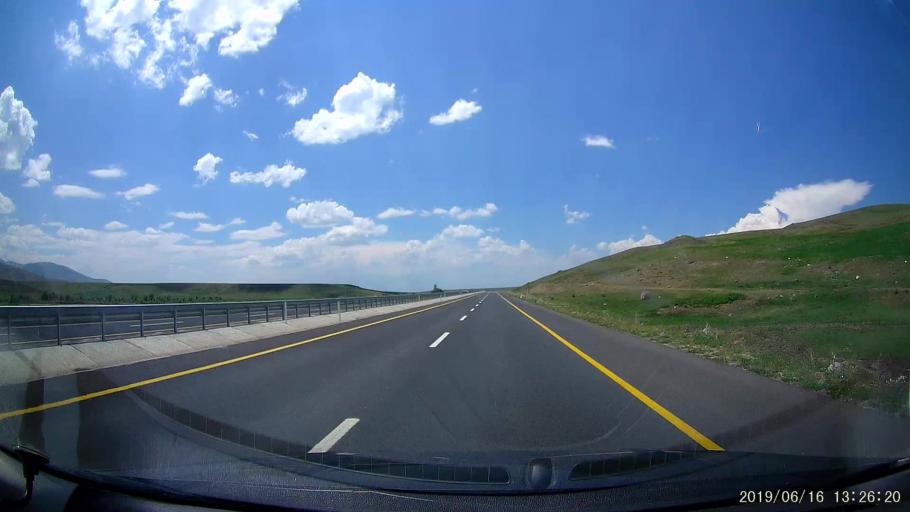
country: TR
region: Agri
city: Taslicay
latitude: 39.6584
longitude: 43.3308
